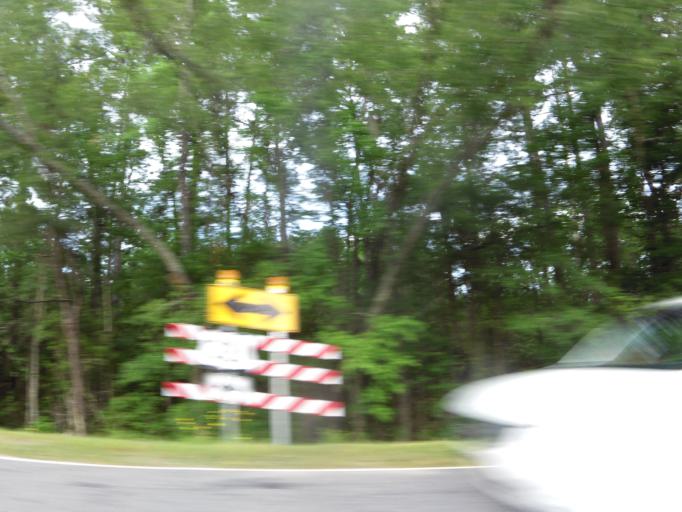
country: US
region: South Carolina
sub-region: Jasper County
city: Ridgeland
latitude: 32.4358
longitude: -81.1039
